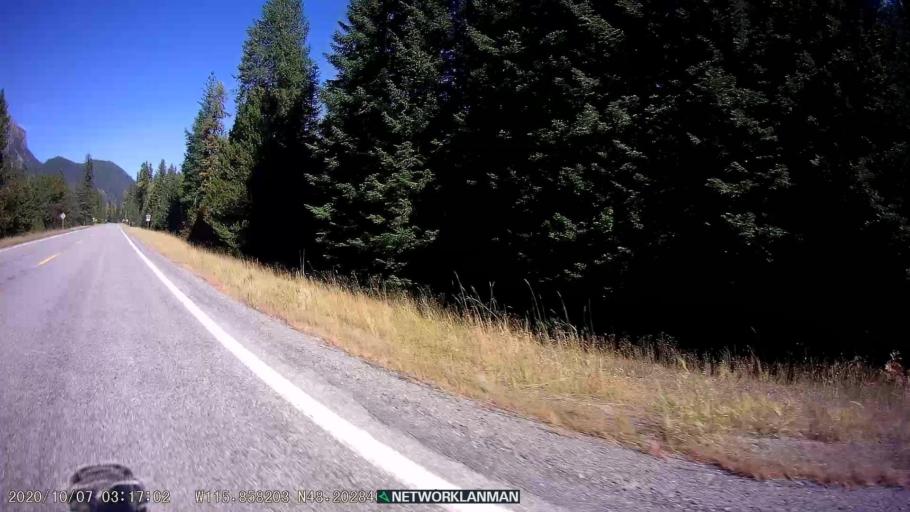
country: US
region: Montana
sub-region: Lincoln County
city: Libby
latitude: 48.2031
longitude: -115.8582
